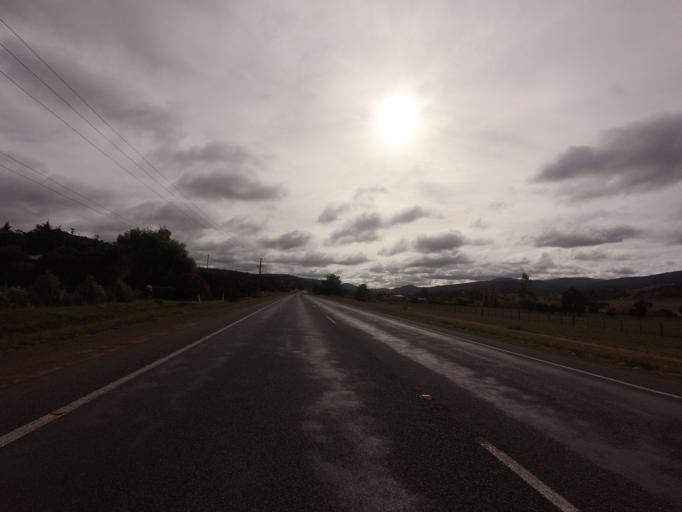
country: AU
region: Tasmania
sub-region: Brighton
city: Bridgewater
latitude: -42.6385
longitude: 147.2277
